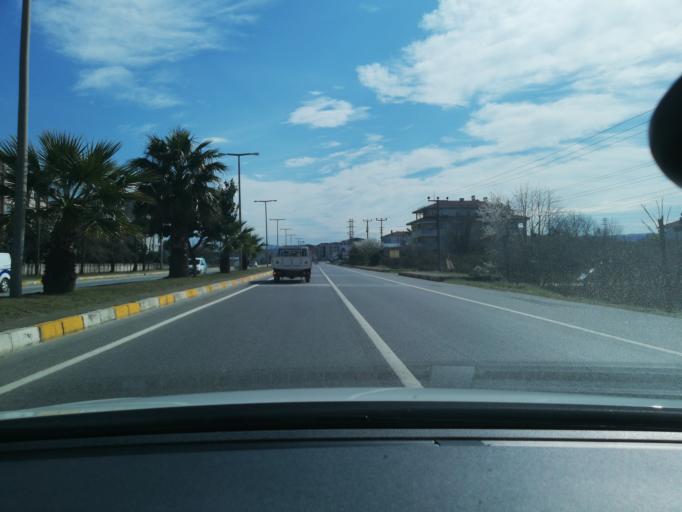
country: TR
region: Duzce
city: Akcakoca
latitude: 41.0853
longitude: 31.1671
